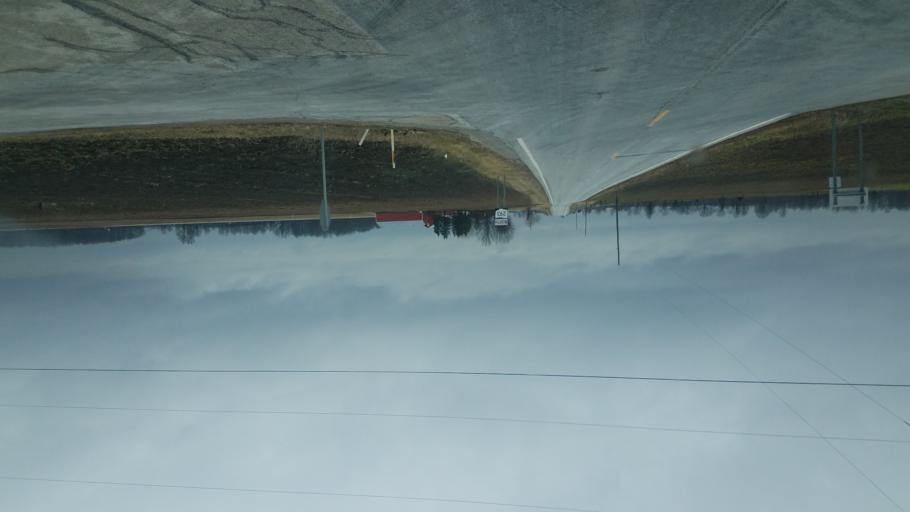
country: US
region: Ohio
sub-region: Hardin County
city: Forest
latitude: 40.8177
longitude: -83.4191
